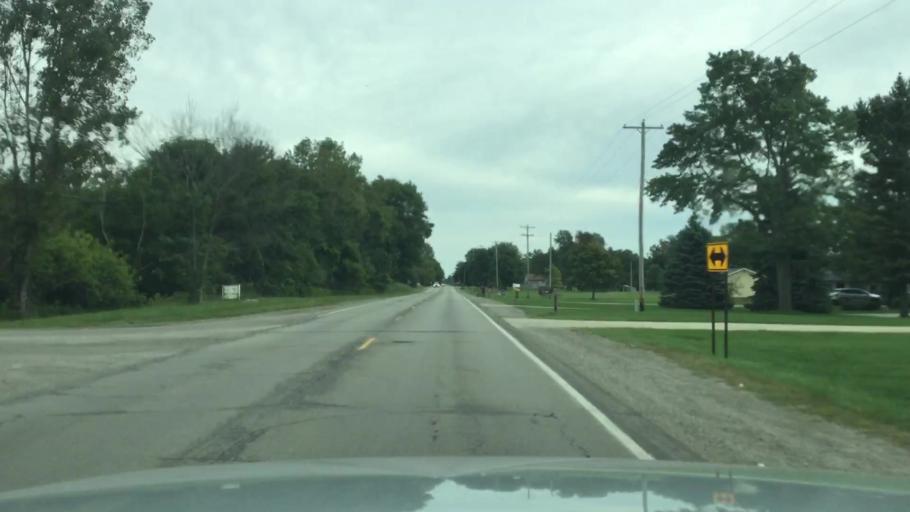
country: US
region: Michigan
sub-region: Genesee County
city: Swartz Creek
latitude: 42.9570
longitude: -83.8701
